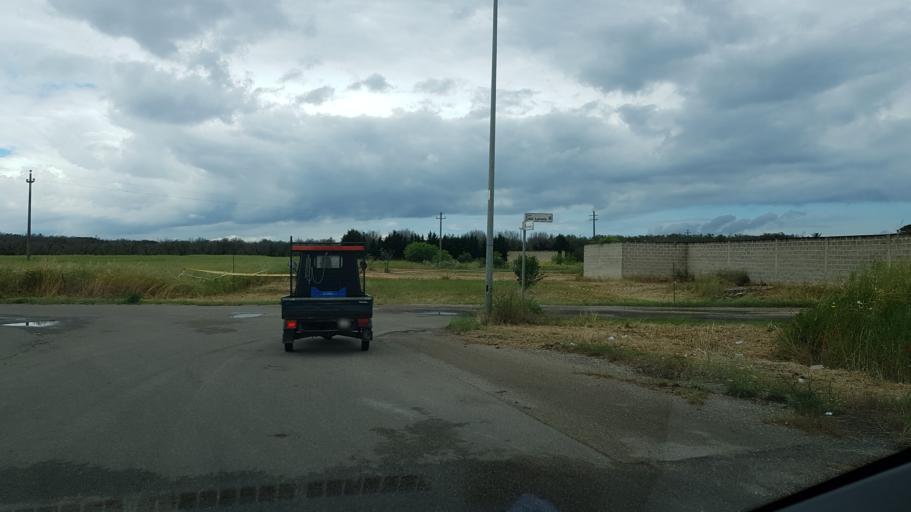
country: IT
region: Apulia
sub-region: Provincia di Brindisi
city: Torchiarolo
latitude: 40.4891
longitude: 18.0436
